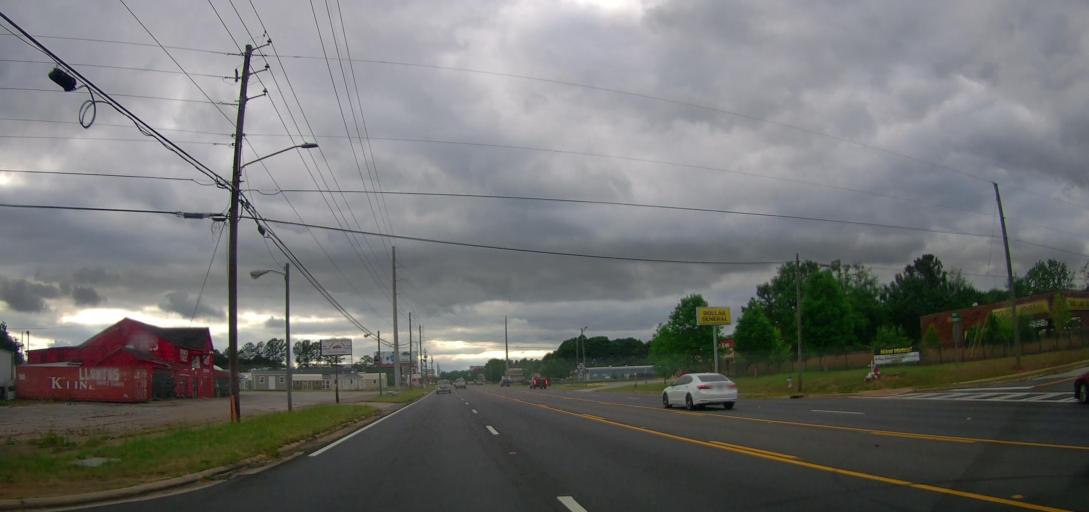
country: US
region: Georgia
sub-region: Oconee County
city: Bogart
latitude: 33.9399
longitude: -83.4949
